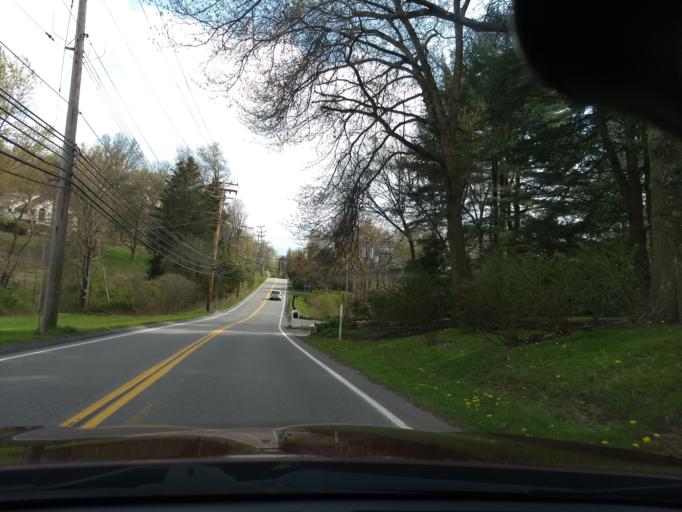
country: US
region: Pennsylvania
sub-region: Allegheny County
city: Fox Chapel
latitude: 40.5328
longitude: -79.8739
